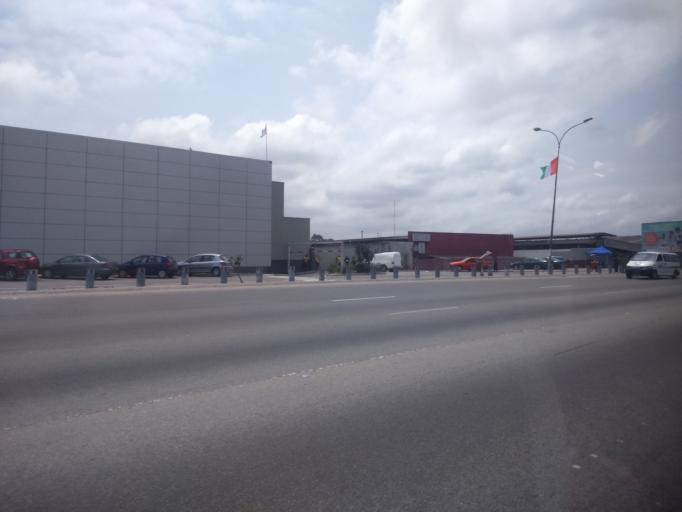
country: CI
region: Lagunes
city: Abidjan
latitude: 5.3015
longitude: -3.9918
